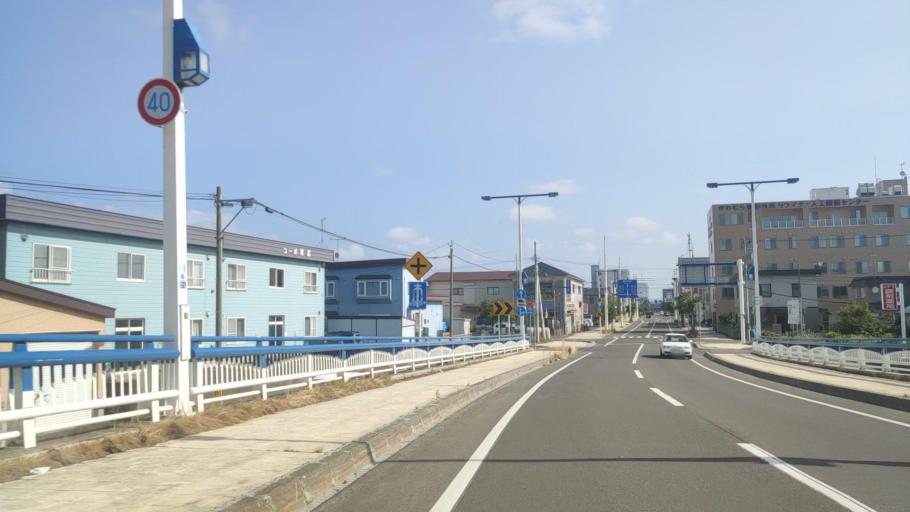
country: JP
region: Hokkaido
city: Shimo-furano
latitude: 43.3398
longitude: 142.3854
